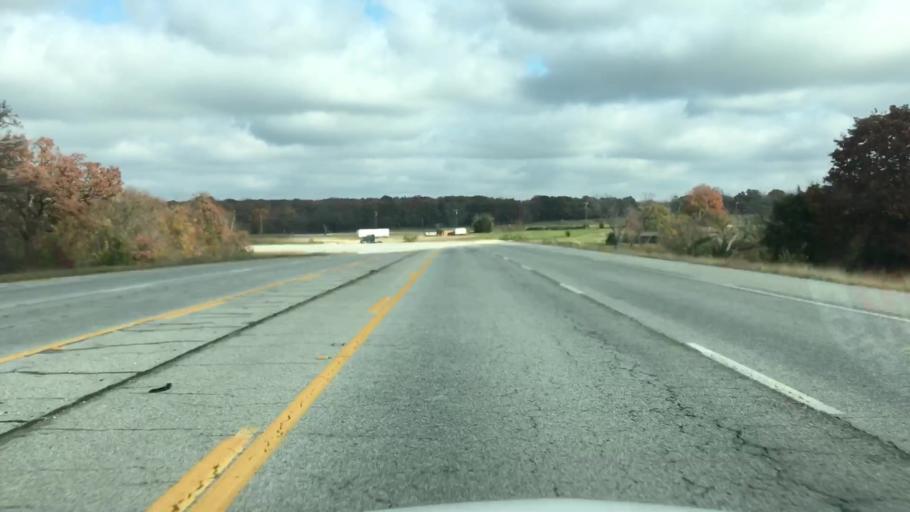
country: US
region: Arkansas
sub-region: Benton County
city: Gentry
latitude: 36.2351
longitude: -94.4897
